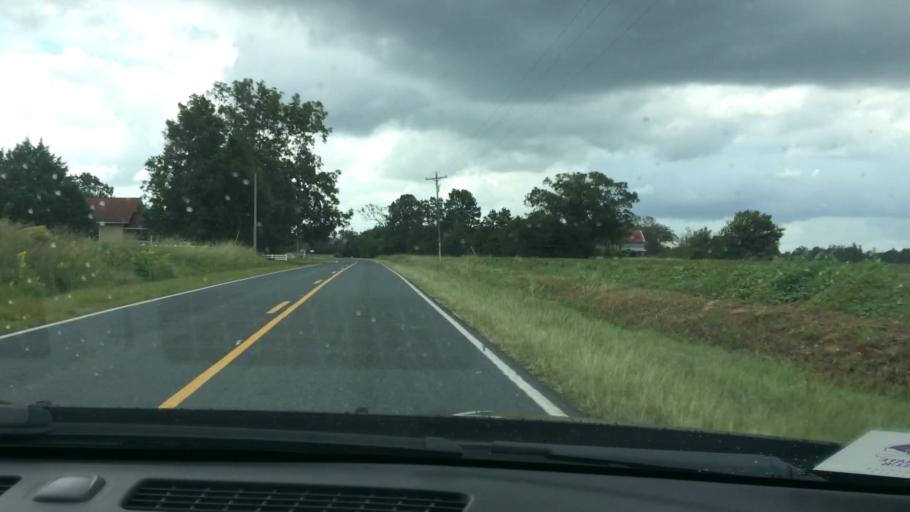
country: US
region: North Carolina
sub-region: Greene County
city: Maury
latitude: 35.5109
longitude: -77.5255
